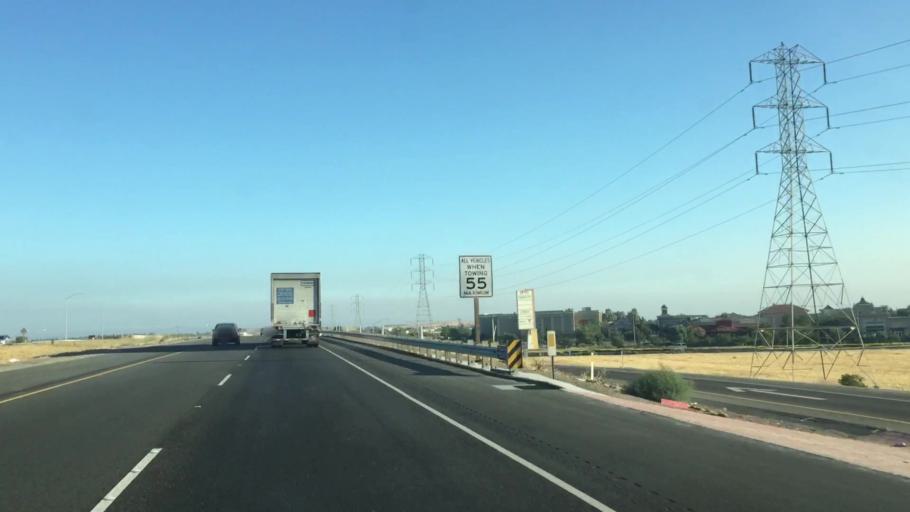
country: US
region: California
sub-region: Contra Costa County
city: Brentwood
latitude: 37.9415
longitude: -121.7404
